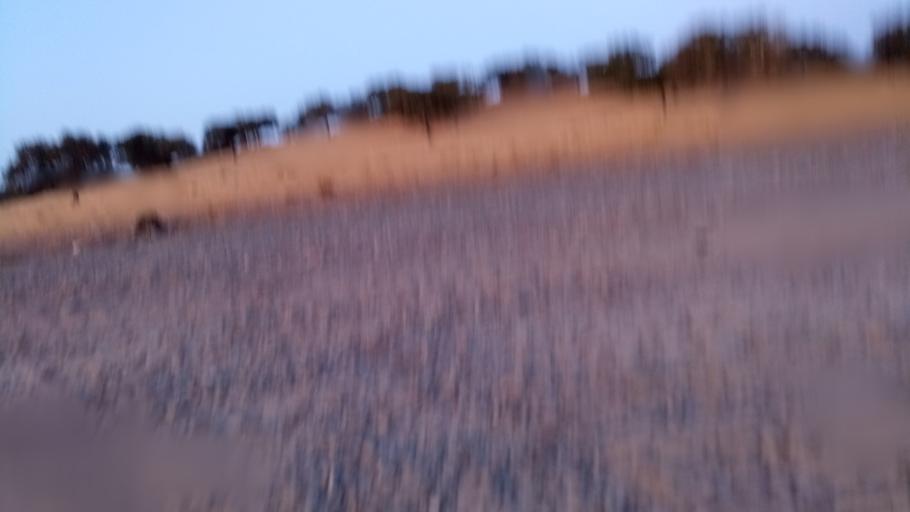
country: PT
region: Evora
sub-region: Mourao
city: Mourao
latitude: 38.3499
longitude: -7.4356
